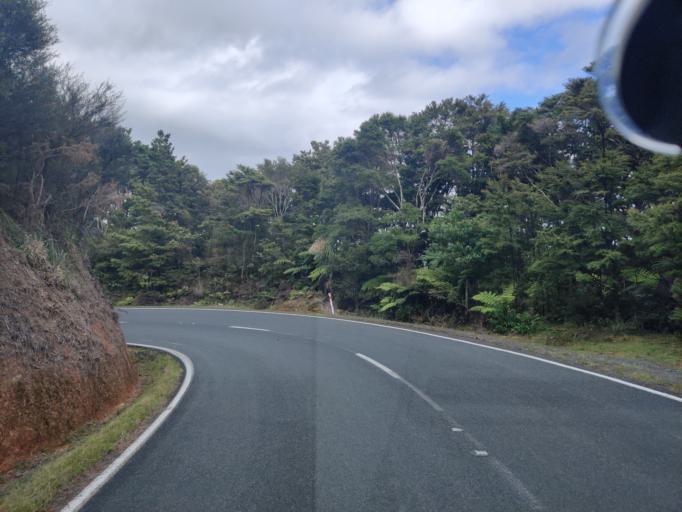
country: NZ
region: Northland
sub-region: Whangarei
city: Ngunguru
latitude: -35.5781
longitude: 174.4055
